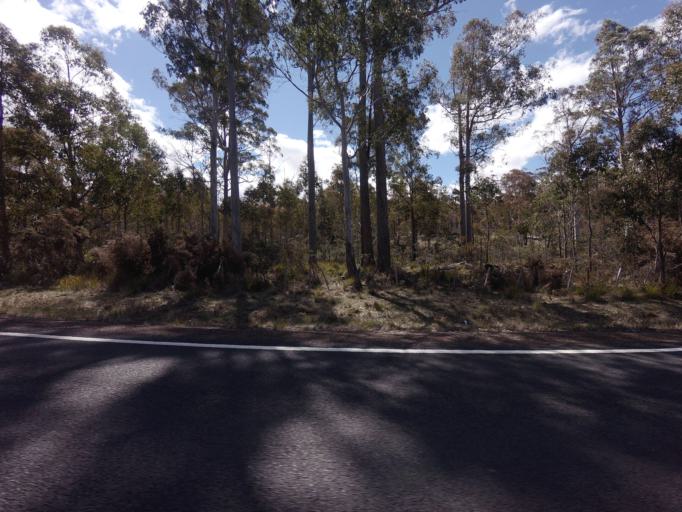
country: AU
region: Tasmania
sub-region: Northern Midlands
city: Evandale
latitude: -42.0341
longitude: 147.8192
